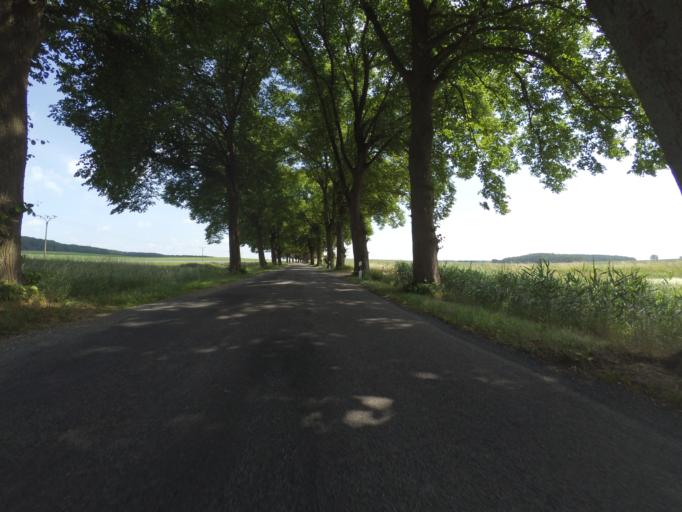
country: DE
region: Mecklenburg-Vorpommern
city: Lubz
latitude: 53.4534
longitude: 12.0510
